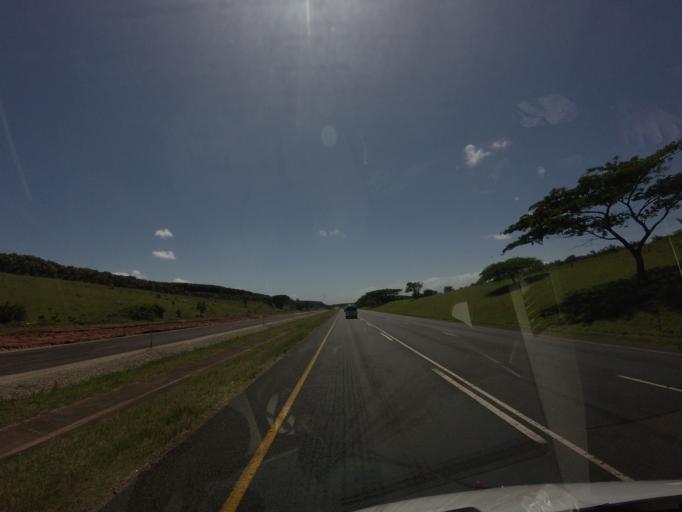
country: ZA
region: KwaZulu-Natal
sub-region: uThungulu District Municipality
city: eSikhawini
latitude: -28.8905
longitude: 31.8449
